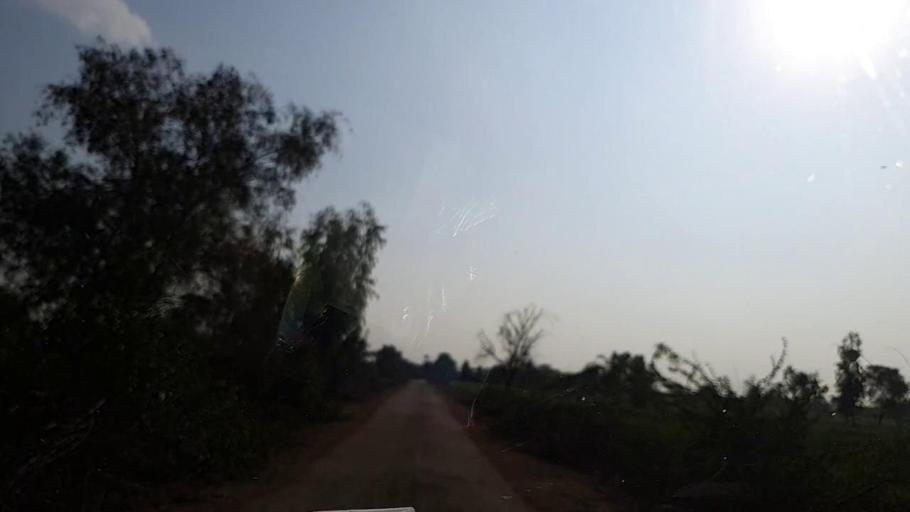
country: PK
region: Sindh
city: Nawabshah
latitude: 26.1466
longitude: 68.3902
